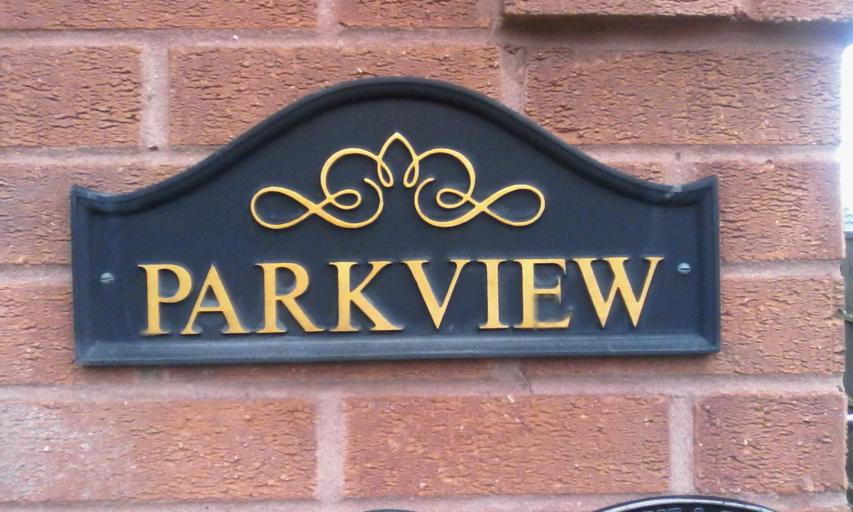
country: GB
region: England
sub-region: Nottinghamshire
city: Arnold
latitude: 52.9752
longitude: -1.1118
